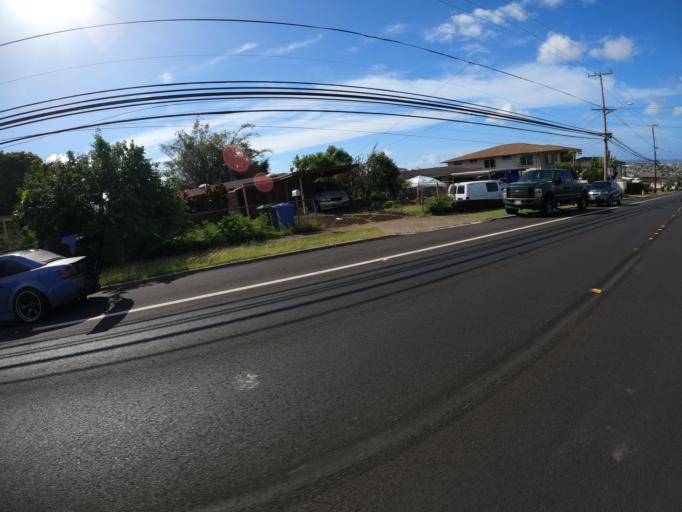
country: US
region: Hawaii
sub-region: Honolulu County
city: Halawa Heights
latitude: 21.3798
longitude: -157.9152
